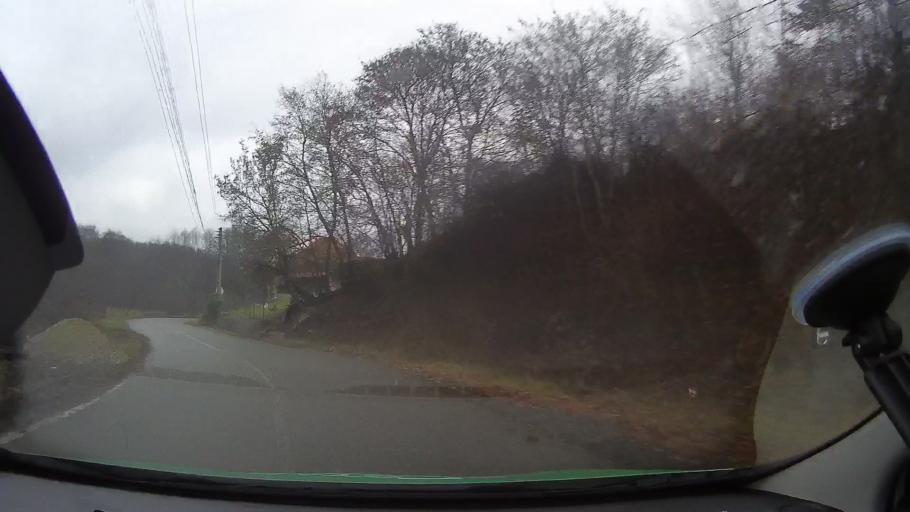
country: RO
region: Hunedoara
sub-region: Comuna Tomesti
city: Tomesti
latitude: 46.2041
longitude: 22.6618
